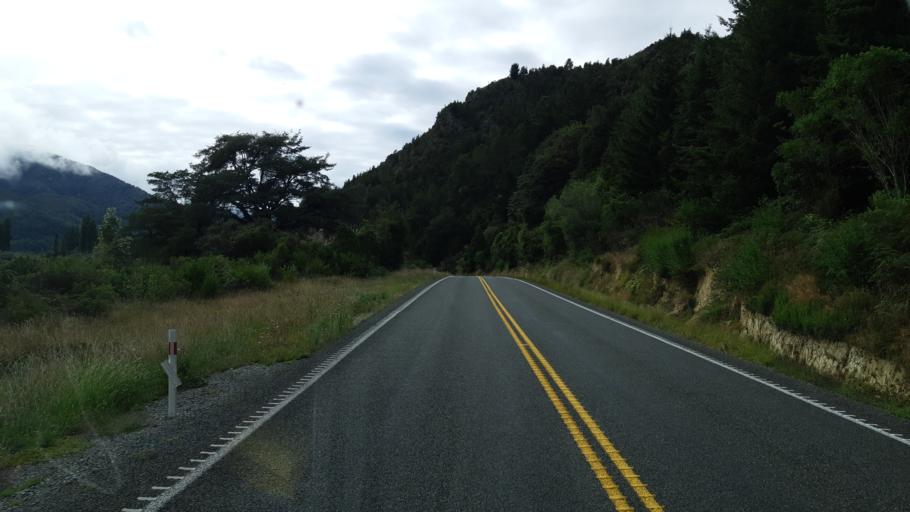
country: NZ
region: West Coast
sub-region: Buller District
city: Westport
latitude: -41.7818
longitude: 172.2652
